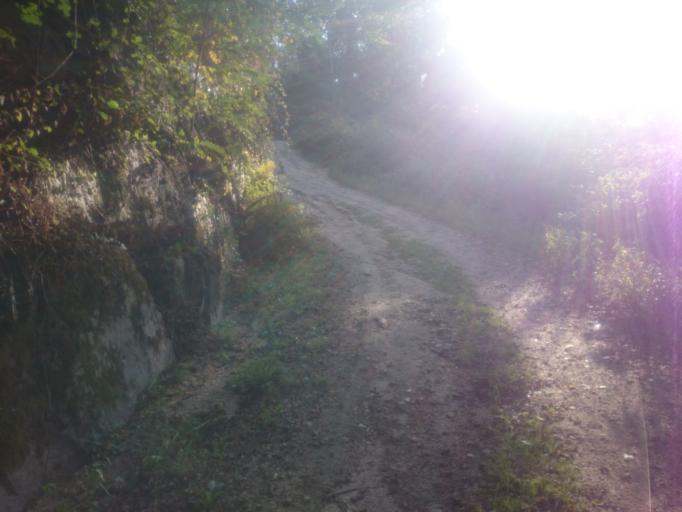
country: ES
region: Galicia
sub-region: Provincia de Pontevedra
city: Porrino
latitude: 42.1563
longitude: -8.6109
